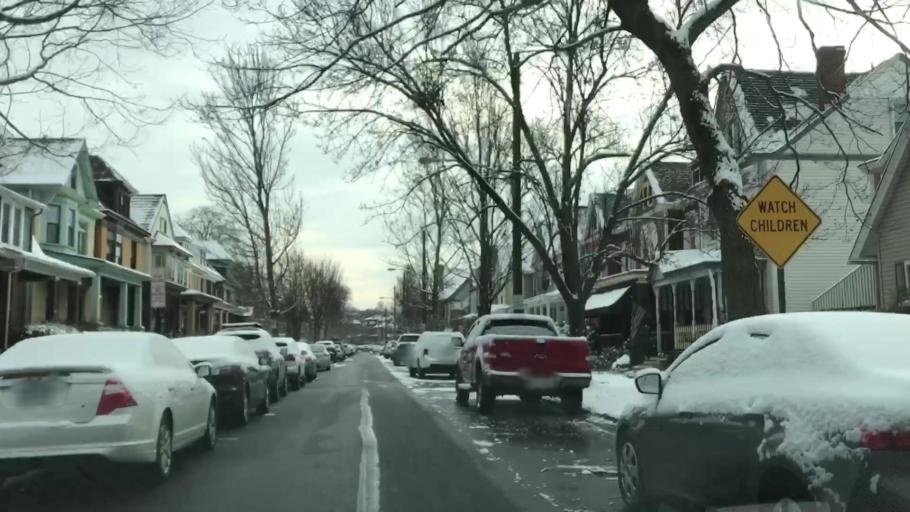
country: US
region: Pennsylvania
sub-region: Allegheny County
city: Aspinwall
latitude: 40.4915
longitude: -79.9046
